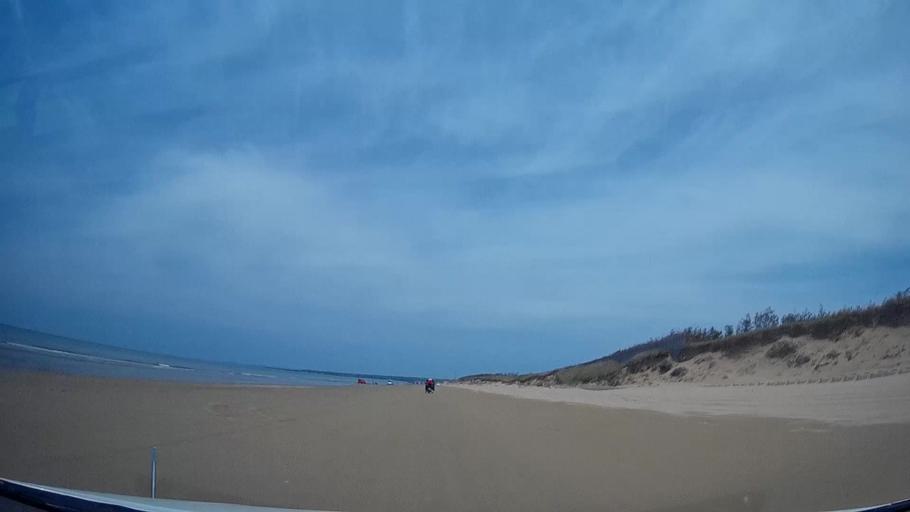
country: JP
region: Ishikawa
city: Hakui
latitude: 36.8569
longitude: 136.7554
